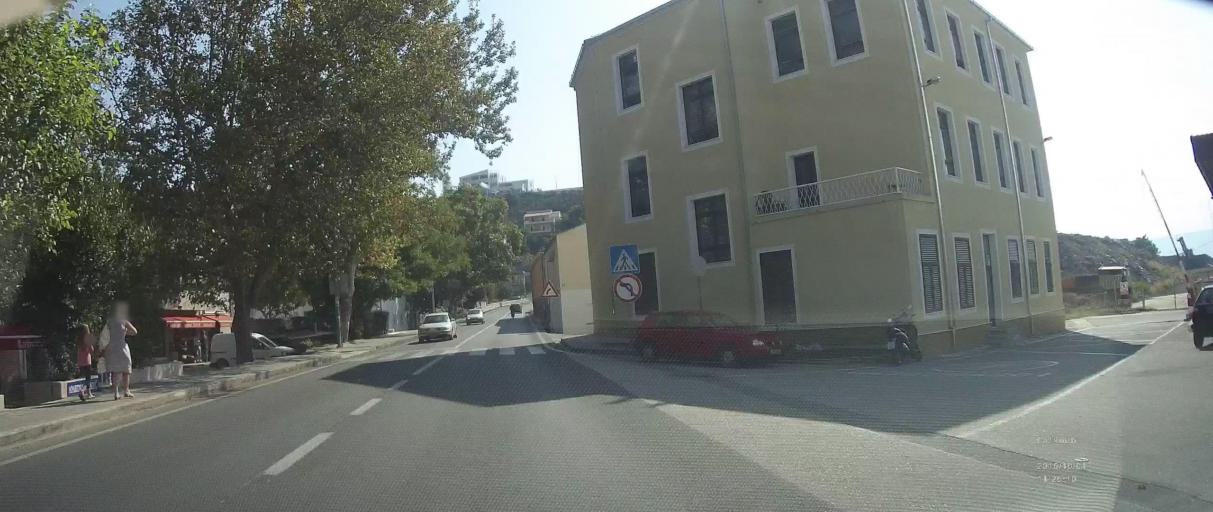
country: HR
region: Splitsko-Dalmatinska
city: Duce
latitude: 43.4438
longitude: 16.6417
